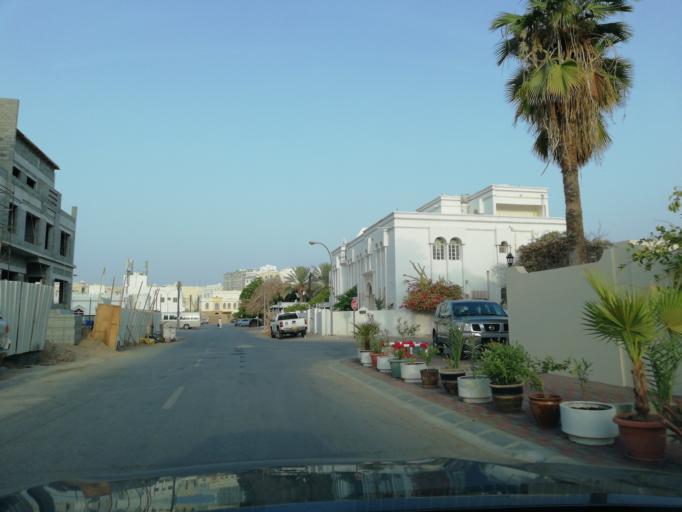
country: OM
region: Muhafazat Masqat
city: Bawshar
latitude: 23.5942
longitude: 58.3985
